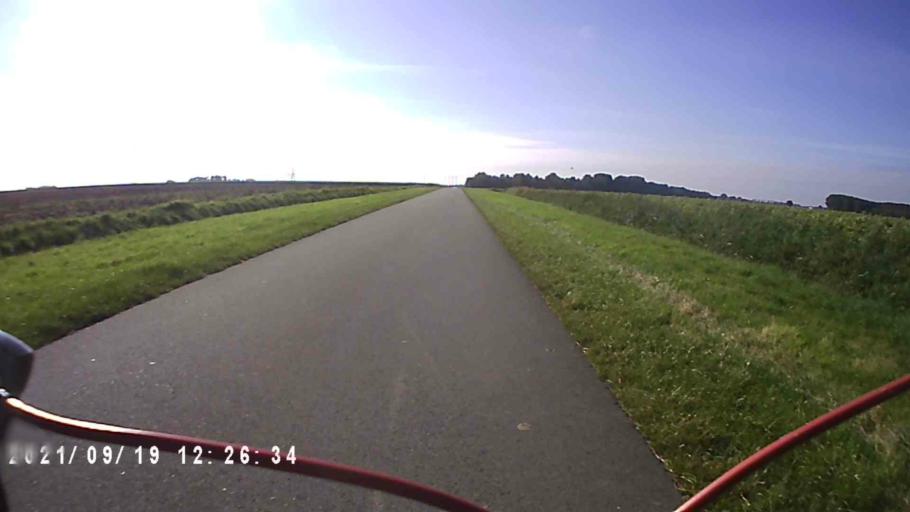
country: NL
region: Groningen
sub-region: Gemeente Slochteren
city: Slochteren
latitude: 53.2335
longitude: 6.8920
